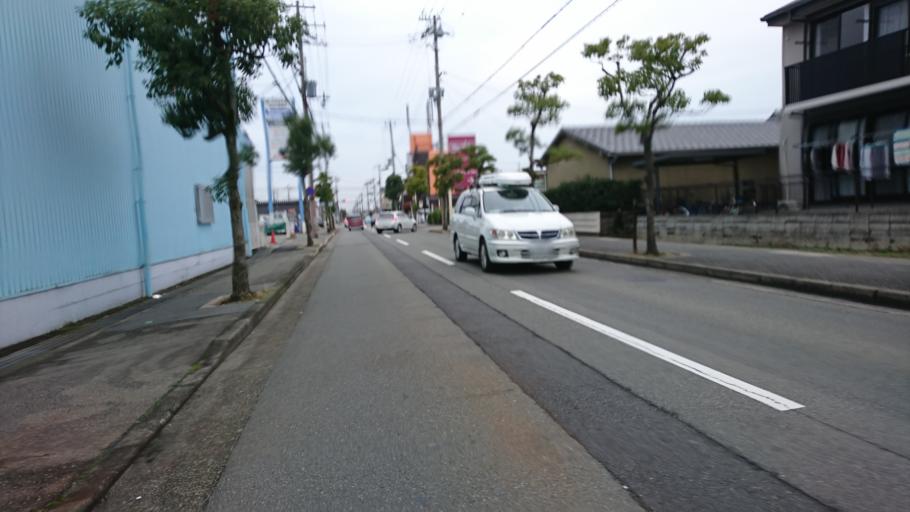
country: JP
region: Hyogo
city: Kakogawacho-honmachi
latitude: 34.7664
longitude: 134.8213
